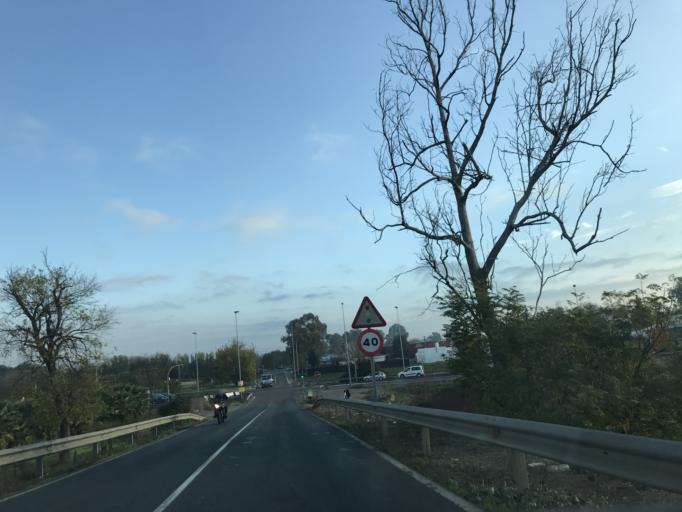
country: ES
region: Andalusia
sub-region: Provincia de Sevilla
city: Sevilla
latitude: 37.4219
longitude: -5.9481
